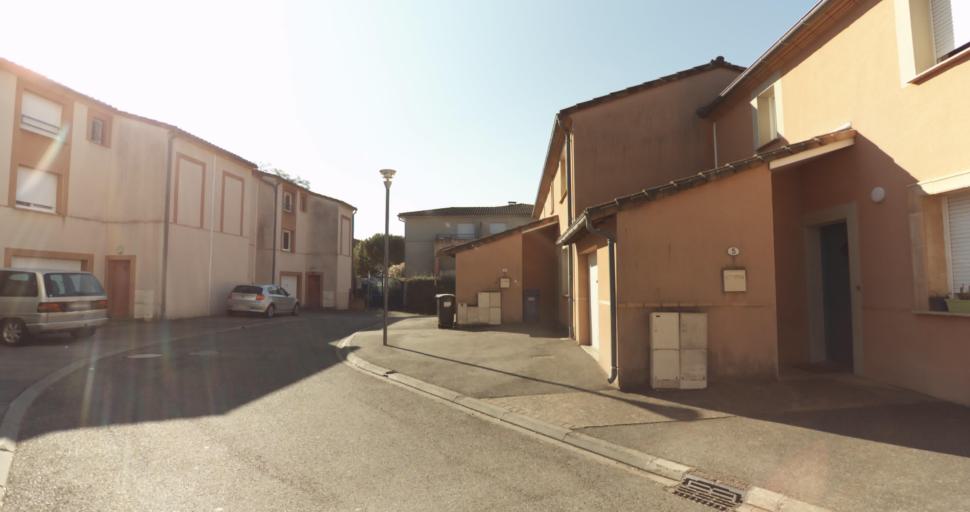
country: FR
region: Midi-Pyrenees
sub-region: Departement de la Haute-Garonne
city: L'Union
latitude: 43.6650
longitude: 1.4806
